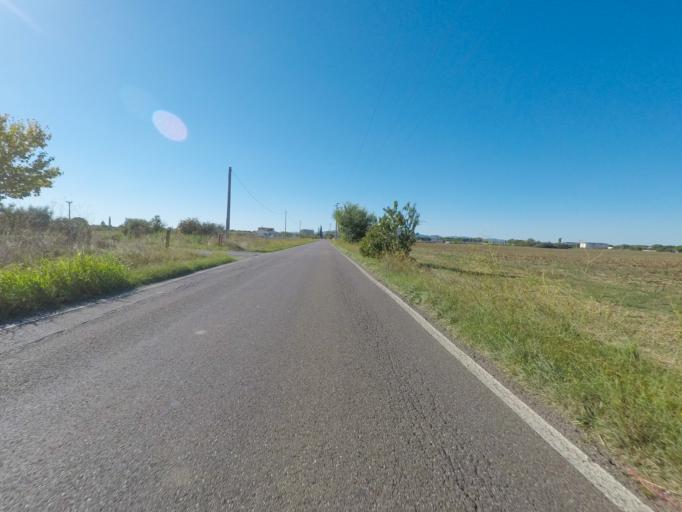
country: IT
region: Tuscany
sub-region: Provincia di Grosseto
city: Grosseto
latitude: 42.7738
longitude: 11.1361
